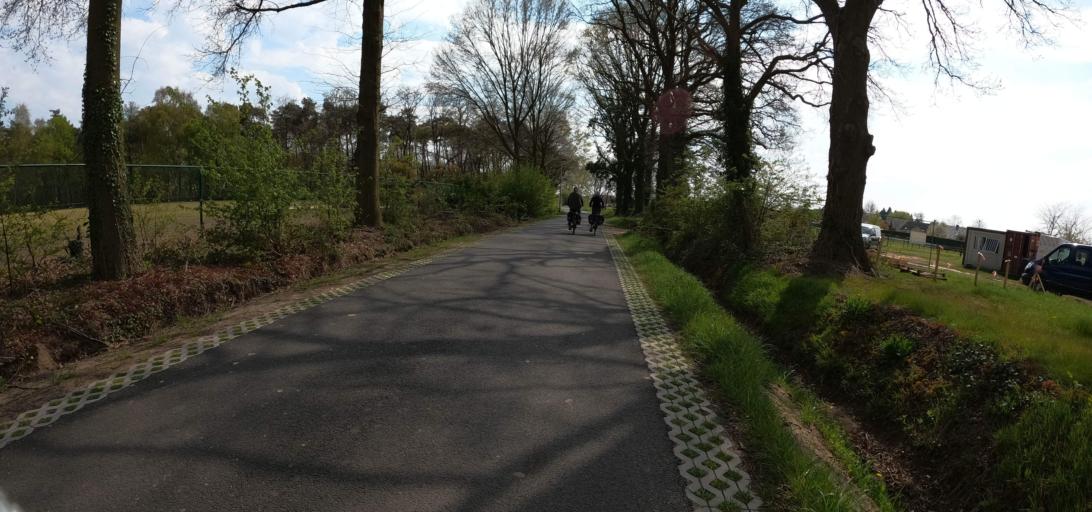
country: BE
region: Flanders
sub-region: Provincie Antwerpen
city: Oostmalle
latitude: 51.3071
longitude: 4.7477
